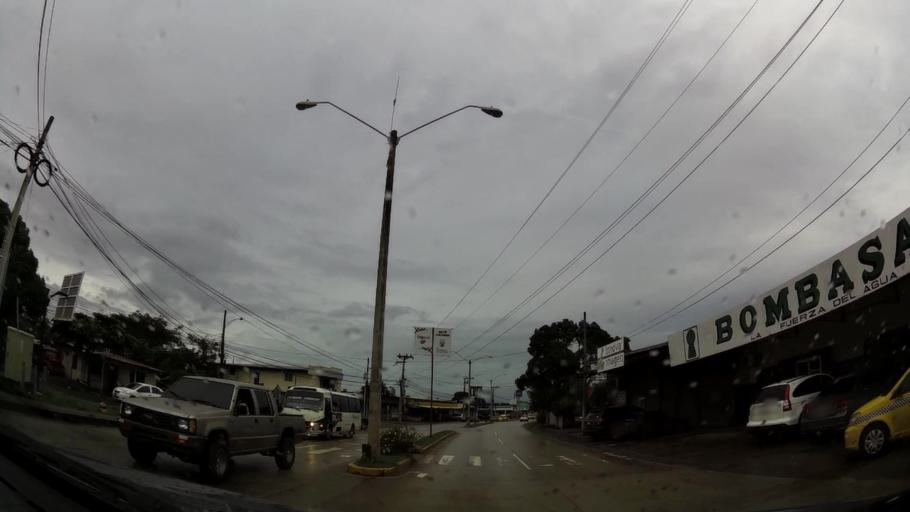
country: PA
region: Veraguas
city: Santiago de Veraguas
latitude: 8.0999
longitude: -80.9692
